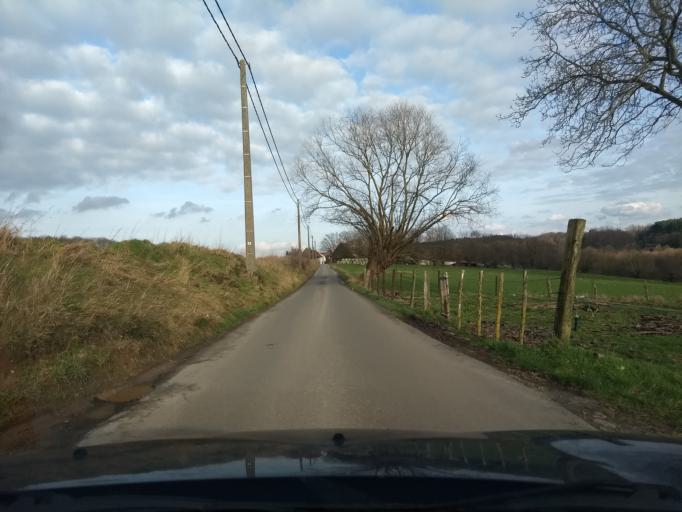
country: BE
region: Wallonia
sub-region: Province du Brabant Wallon
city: Braine-le-Chateau
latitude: 50.6935
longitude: 4.2528
